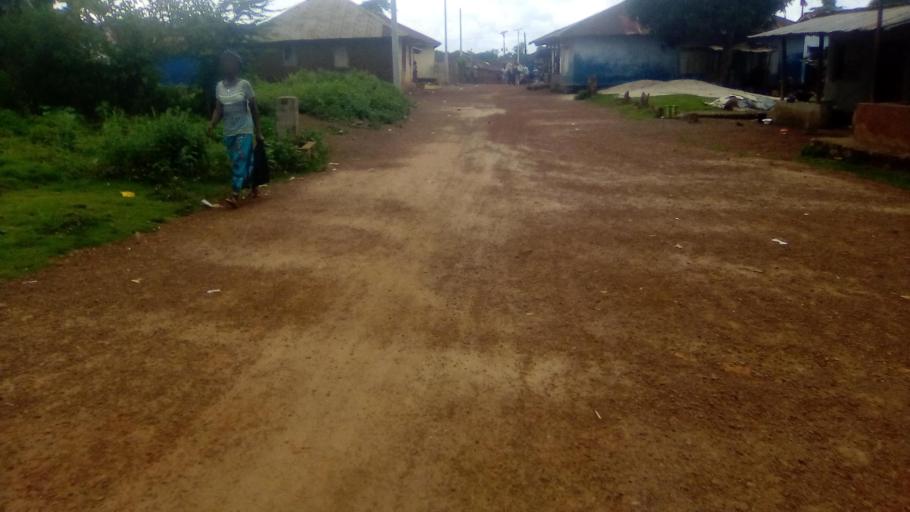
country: SL
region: Southern Province
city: Moyamba
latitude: 8.1567
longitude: -12.4287
